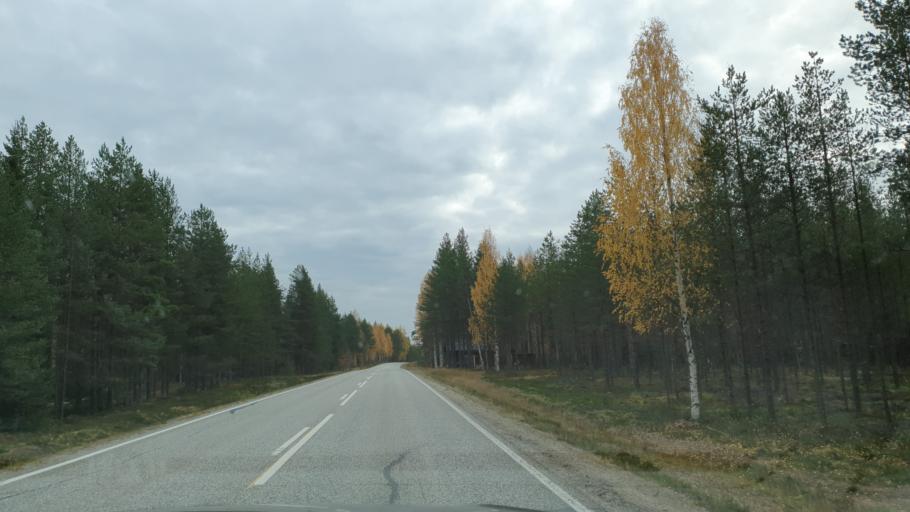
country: FI
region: Kainuu
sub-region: Kehys-Kainuu
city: Puolanka
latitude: 65.2392
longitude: 27.5862
